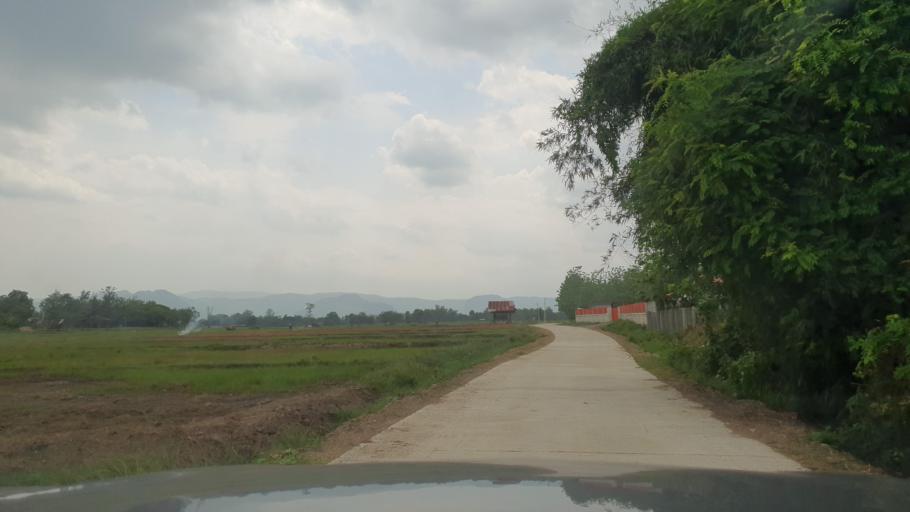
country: TH
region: Sukhothai
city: Thung Saliam
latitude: 17.3294
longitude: 99.4491
